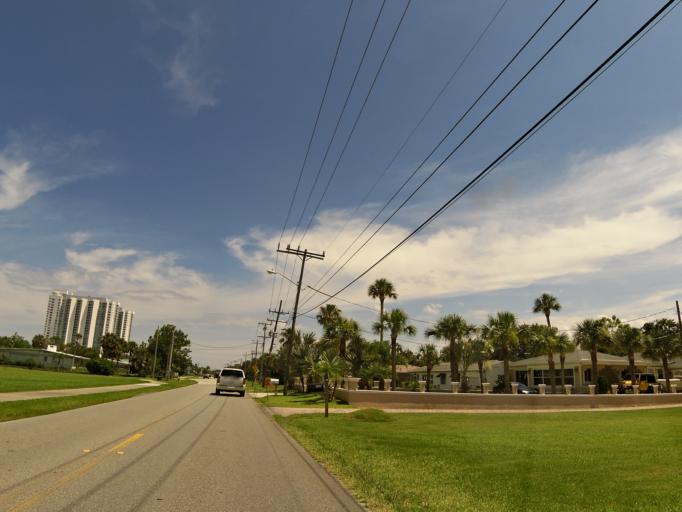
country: US
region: Florida
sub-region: Volusia County
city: Holly Hill
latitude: 29.2369
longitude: -81.0317
